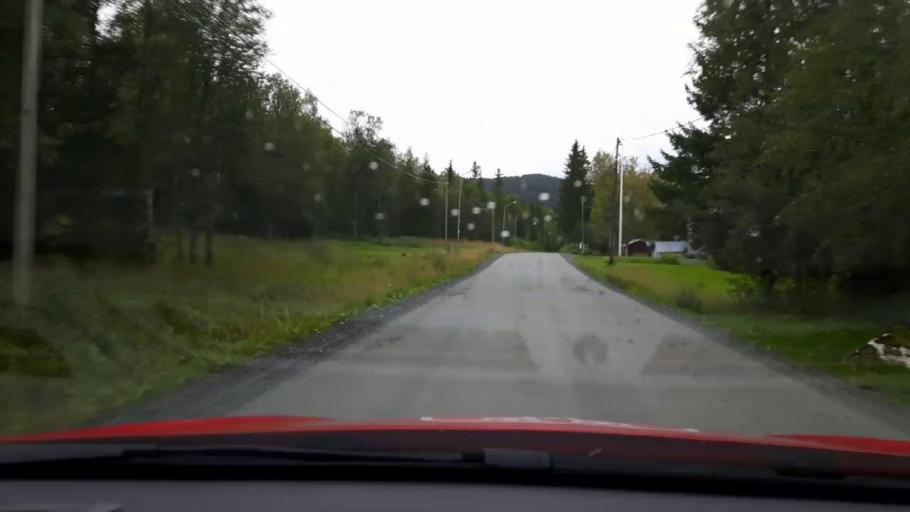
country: SE
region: Jaemtland
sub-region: Are Kommun
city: Are
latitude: 63.4875
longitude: 13.1323
